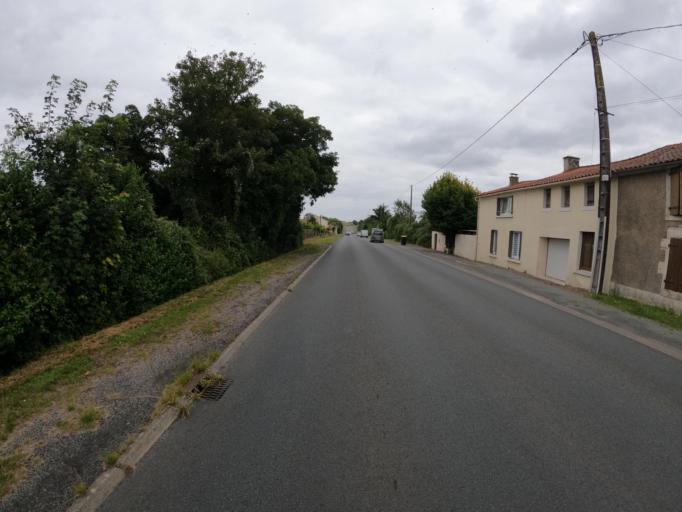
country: FR
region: Pays de la Loire
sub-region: Departement de la Vendee
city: Serigne
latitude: 46.4711
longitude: -0.8561
